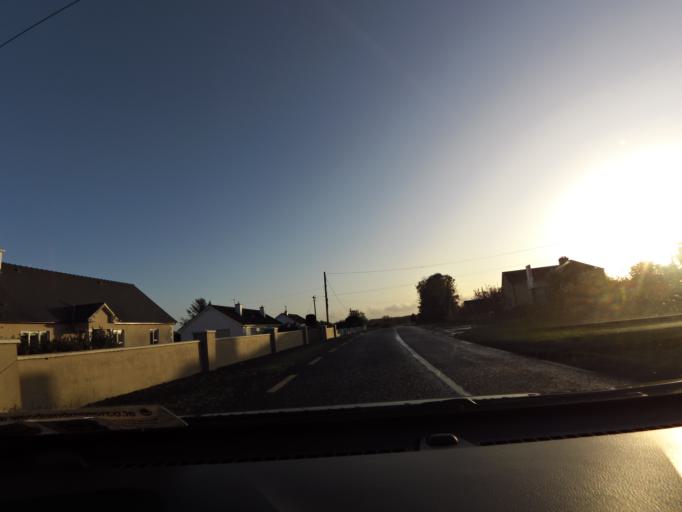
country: IE
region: Connaught
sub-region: Roscommon
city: Castlerea
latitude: 53.7185
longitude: -8.5612
